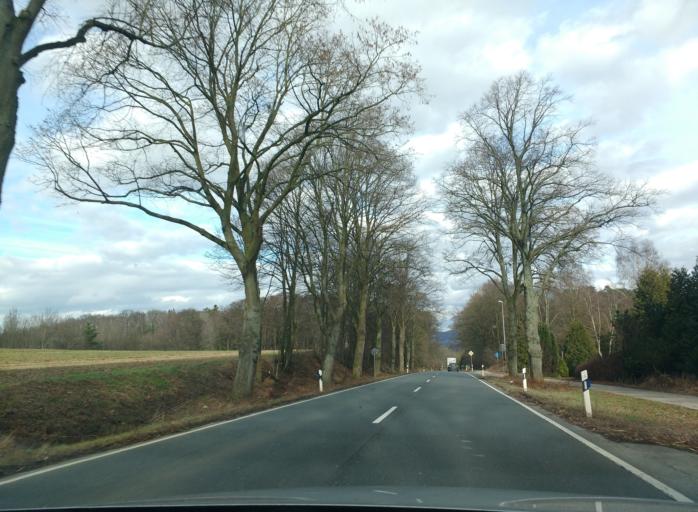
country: DE
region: Lower Saxony
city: Rinteln
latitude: 52.1632
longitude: 9.0227
